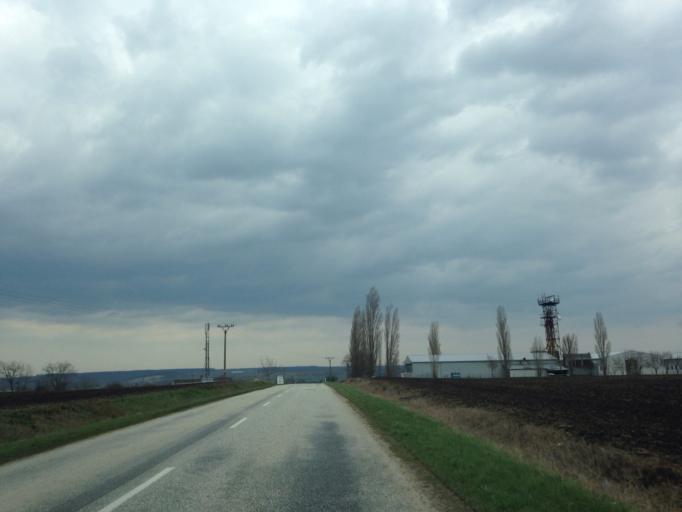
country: SK
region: Nitriansky
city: Svodin
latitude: 47.9830
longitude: 18.3831
